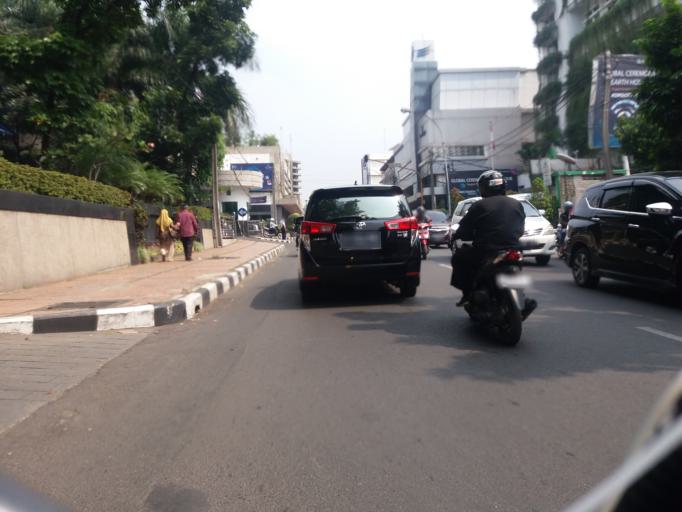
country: ID
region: West Java
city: Bandung
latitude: -6.9200
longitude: 107.6112
